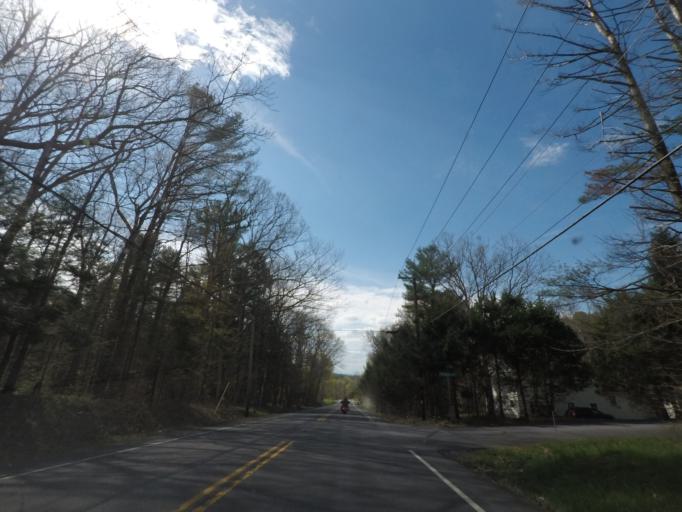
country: US
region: New York
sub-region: Greene County
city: Cairo
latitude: 42.3460
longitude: -74.0376
